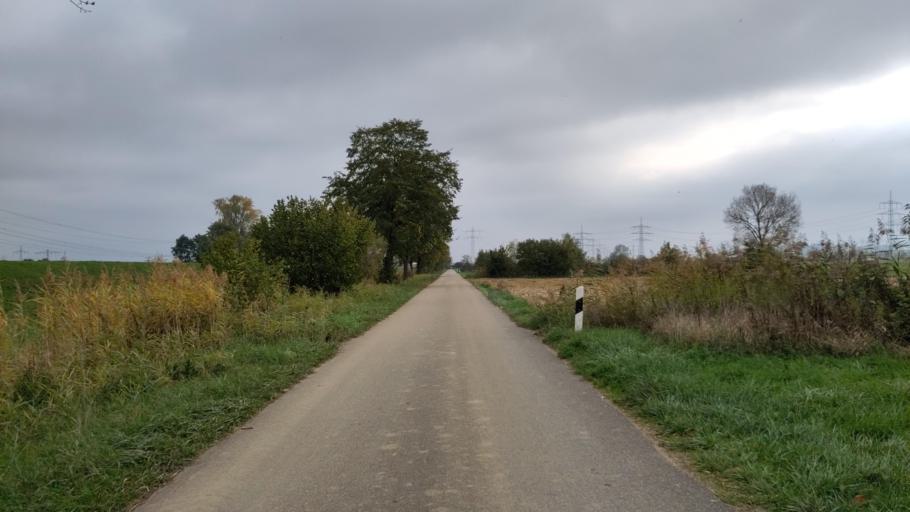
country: DE
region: Baden-Wuerttemberg
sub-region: Freiburg Region
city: Riegel
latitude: 48.1374
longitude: 7.7563
